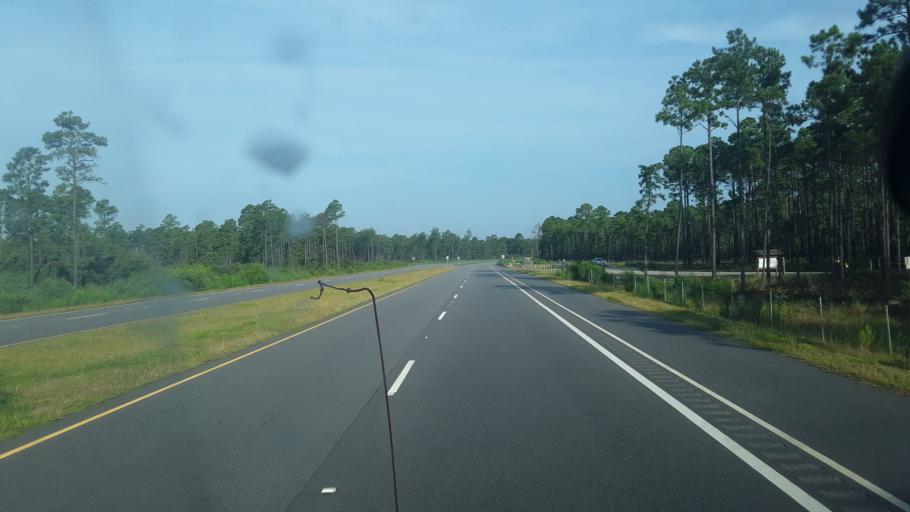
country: US
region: South Carolina
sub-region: Horry County
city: Forestbrook
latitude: 33.8051
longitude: -78.8901
